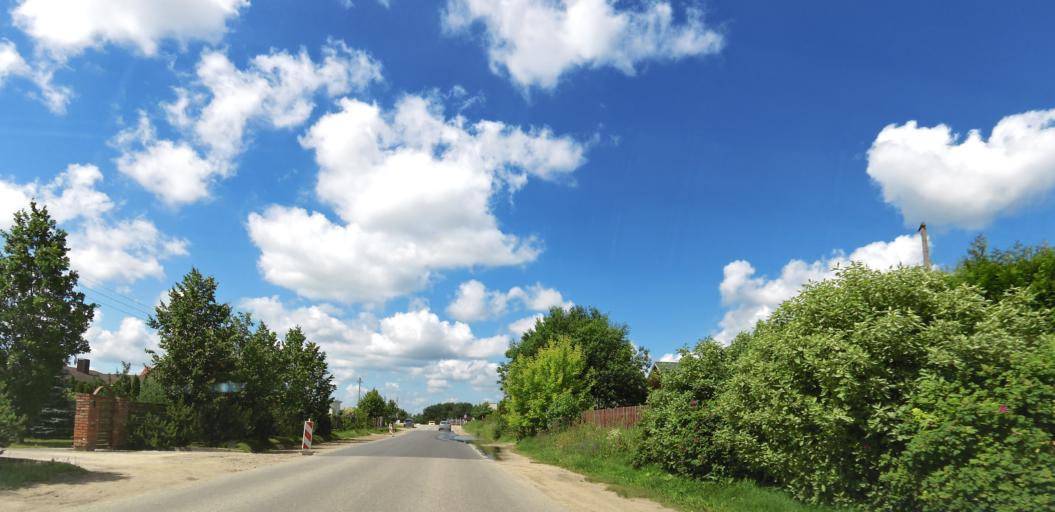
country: LT
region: Vilnius County
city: Pasilaiciai
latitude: 54.7358
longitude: 25.2045
